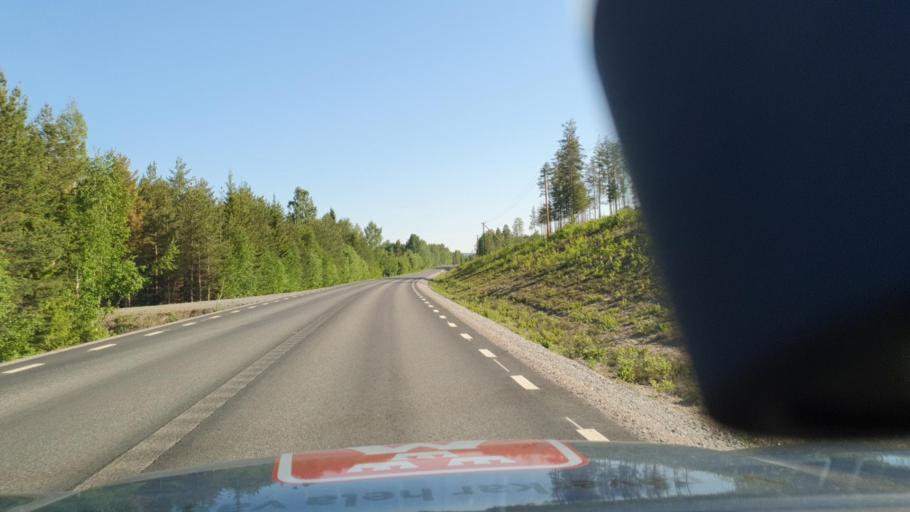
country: SE
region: Norrbotten
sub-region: Alvsbyns Kommun
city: AElvsbyn
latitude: 66.1806
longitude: 20.8774
